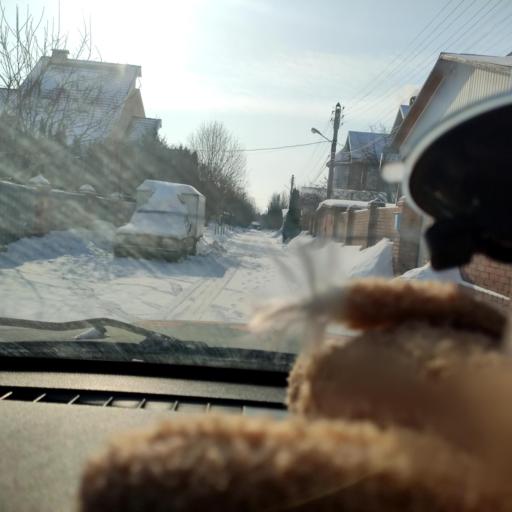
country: RU
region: Samara
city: Podstepki
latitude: 53.5195
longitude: 49.1752
